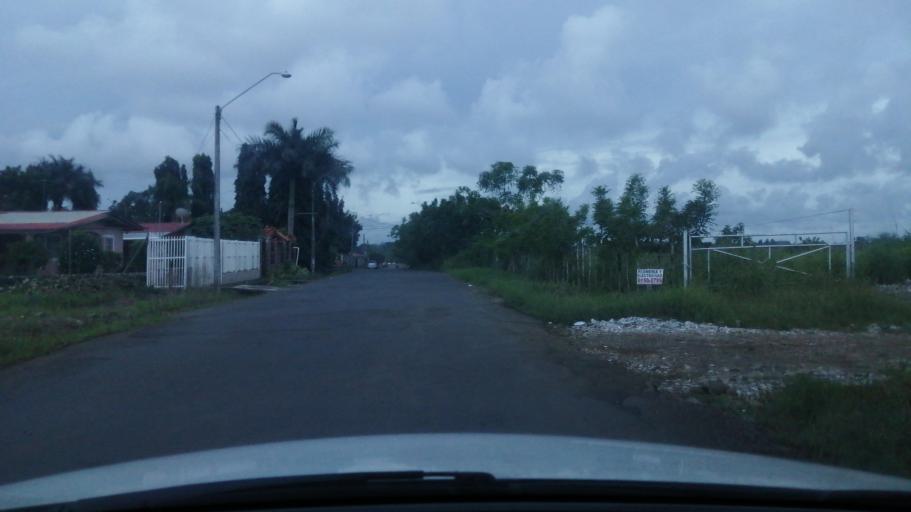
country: PA
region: Chiriqui
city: David
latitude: 8.4051
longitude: -82.4518
